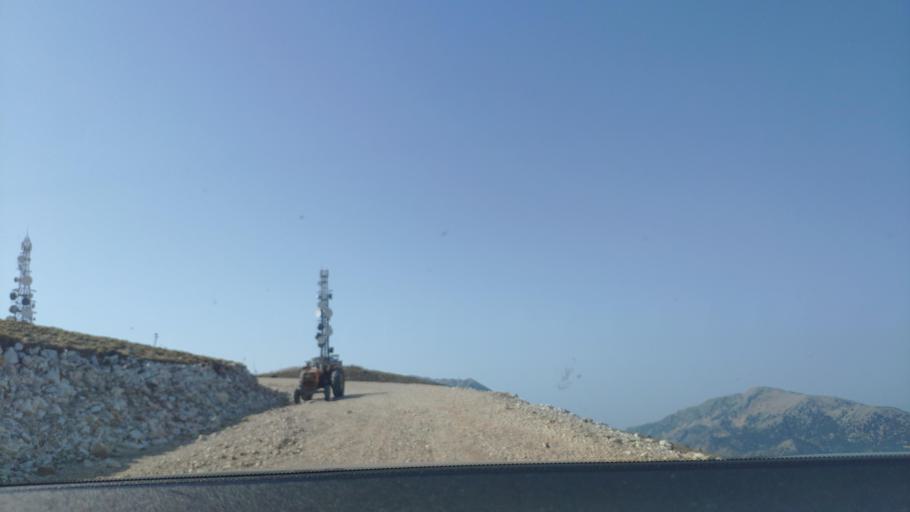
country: GR
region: West Greece
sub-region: Nomos Aitolias kai Akarnanias
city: Monastirakion
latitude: 38.8090
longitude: 20.9799
